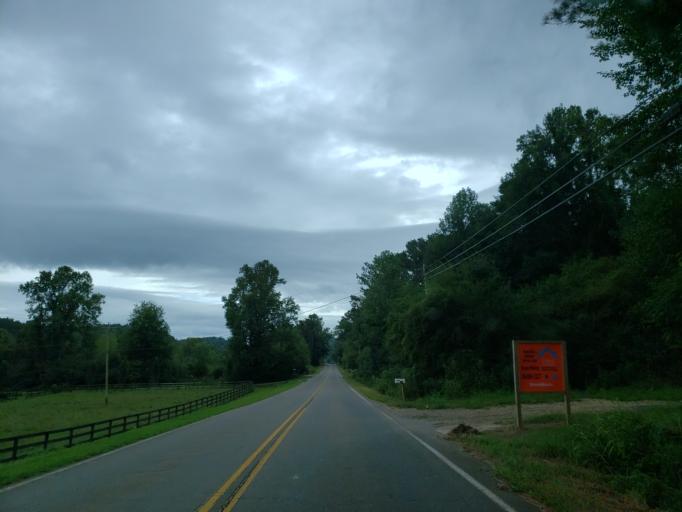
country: US
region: Georgia
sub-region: Gilmer County
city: Ellijay
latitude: 34.5780
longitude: -84.5362
